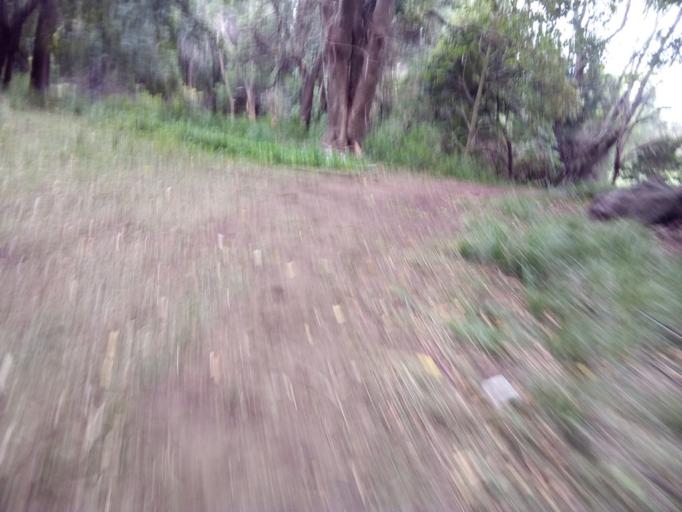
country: AU
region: New South Wales
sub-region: Wollongong
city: Mount Ousley
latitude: -34.3996
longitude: 150.8611
